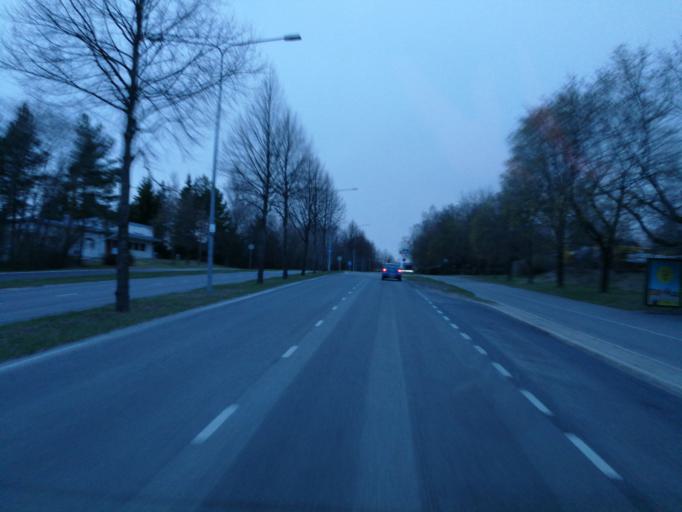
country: FI
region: Varsinais-Suomi
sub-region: Turku
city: Turku
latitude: 60.4645
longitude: 22.2552
